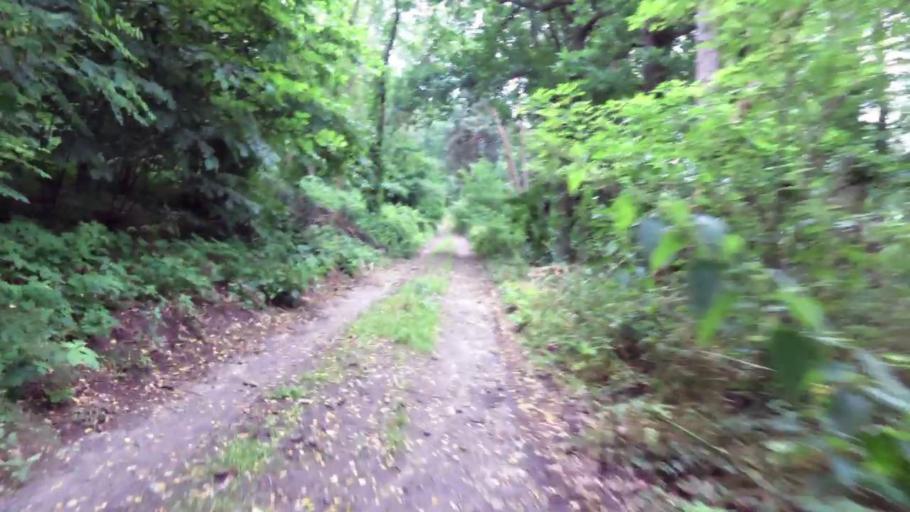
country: PL
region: West Pomeranian Voivodeship
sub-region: Powiat mysliborski
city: Mysliborz
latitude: 52.9648
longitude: 14.9120
